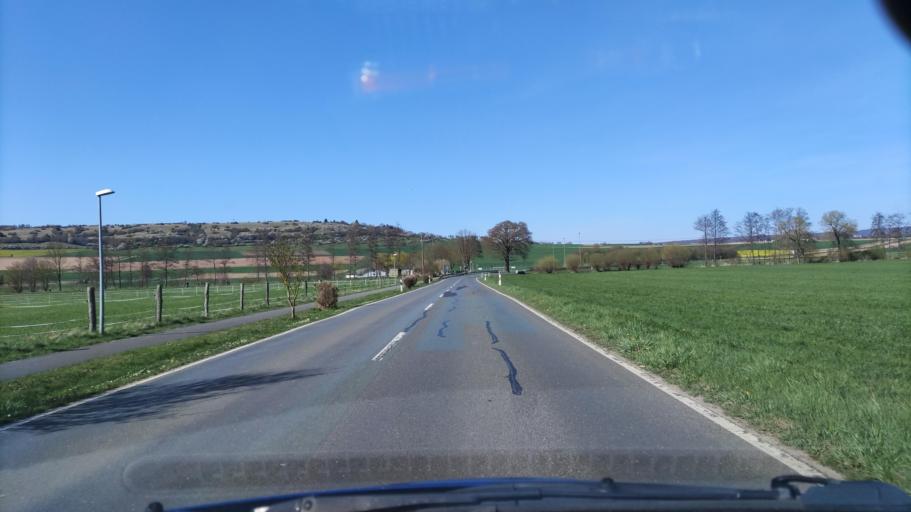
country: DE
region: Hesse
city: Trendelburg
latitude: 51.5963
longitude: 9.4092
